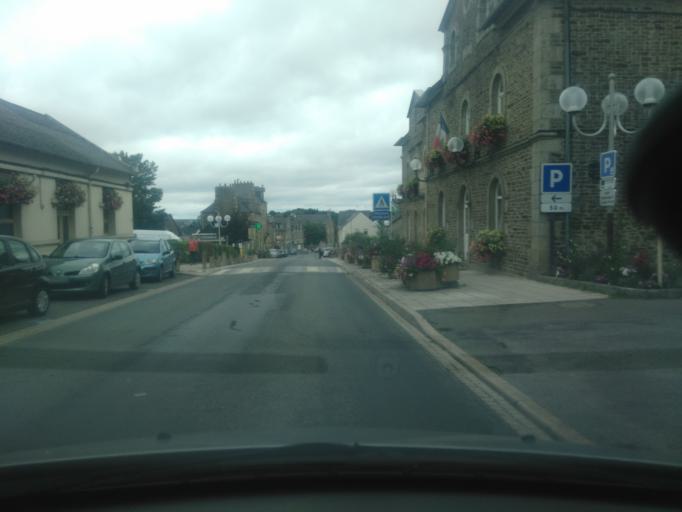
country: FR
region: Brittany
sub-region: Departement des Cotes-d'Armor
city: Lanvallay
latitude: 48.4554
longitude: -2.0279
